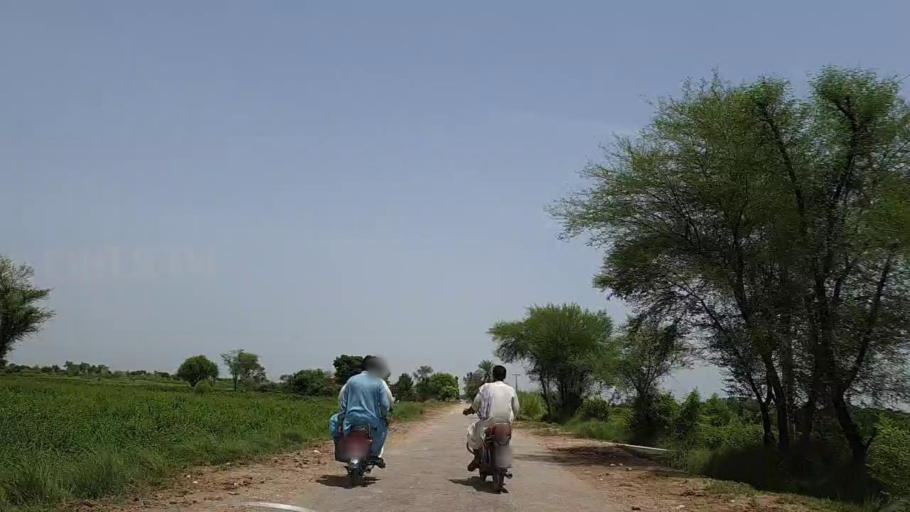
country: PK
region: Sindh
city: Tharu Shah
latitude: 26.9380
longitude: 68.0244
